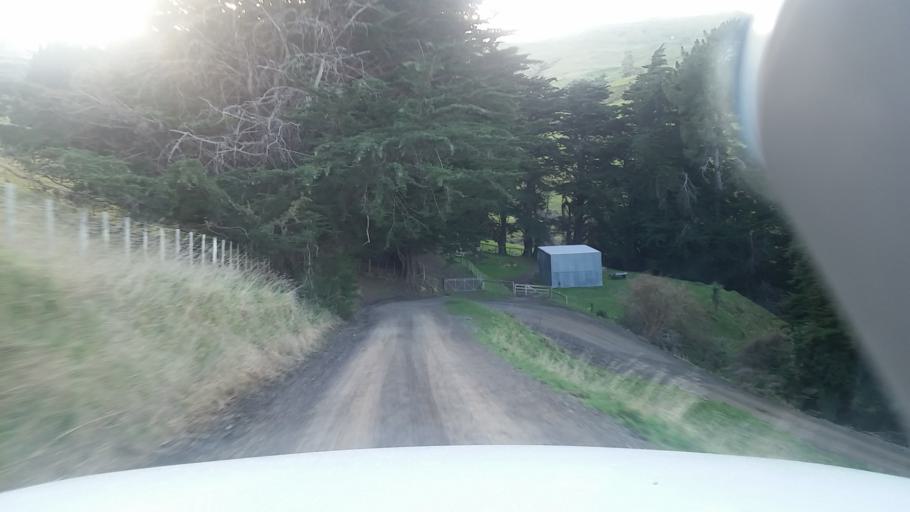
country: NZ
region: Canterbury
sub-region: Christchurch City
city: Christchurch
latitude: -43.7343
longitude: 172.9600
